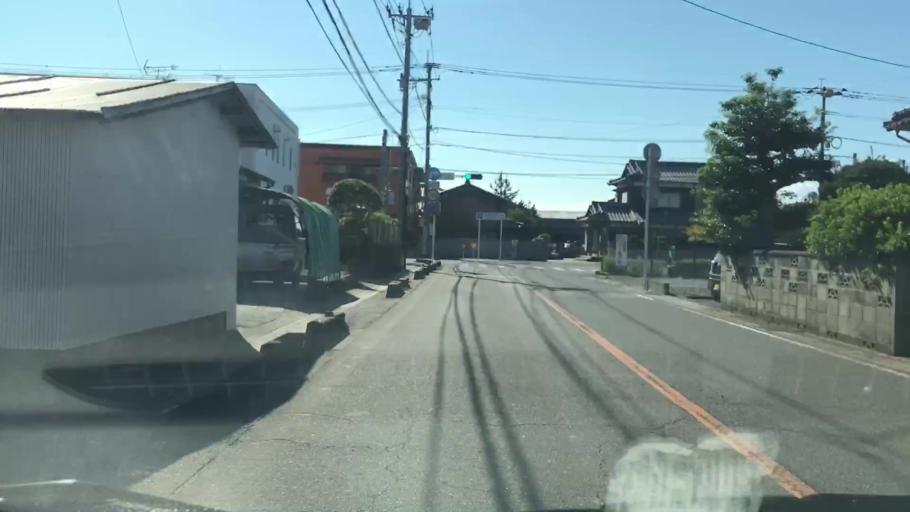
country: JP
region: Saga Prefecture
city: Okawa
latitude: 33.1895
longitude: 130.3200
